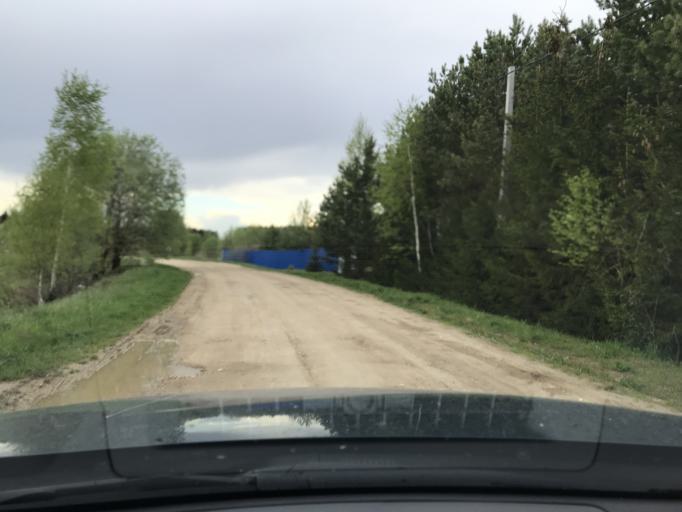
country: RU
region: Moskovskaya
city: Vereya
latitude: 55.3213
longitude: 36.3339
